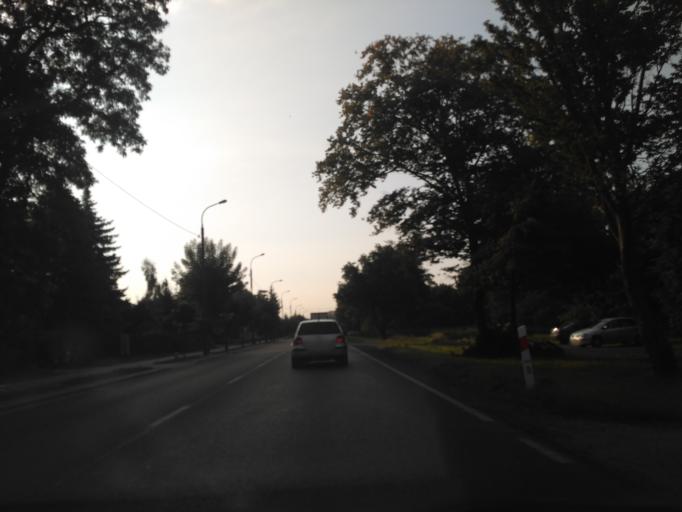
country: PL
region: Lublin Voivodeship
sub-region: Powiat krasnicki
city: Krasnik
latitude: 50.9165
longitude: 22.2428
